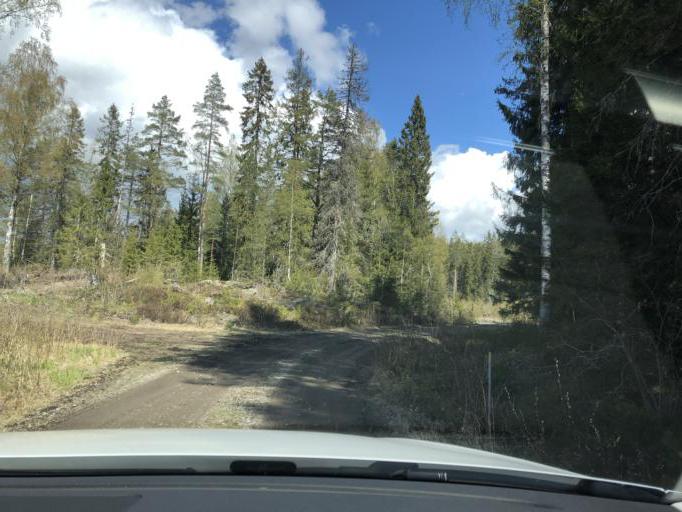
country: SE
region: Dalarna
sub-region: Avesta Kommun
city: Horndal
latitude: 60.2263
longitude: 16.5928
